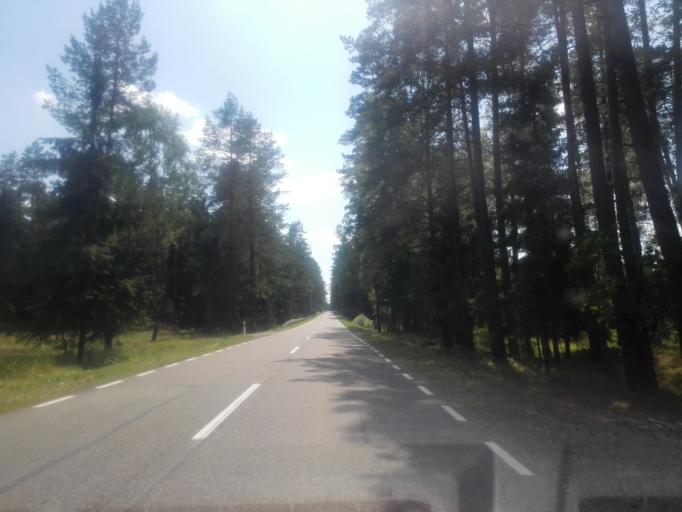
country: PL
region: Podlasie
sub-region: Powiat augustowski
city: Augustow
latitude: 53.9159
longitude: 23.1464
